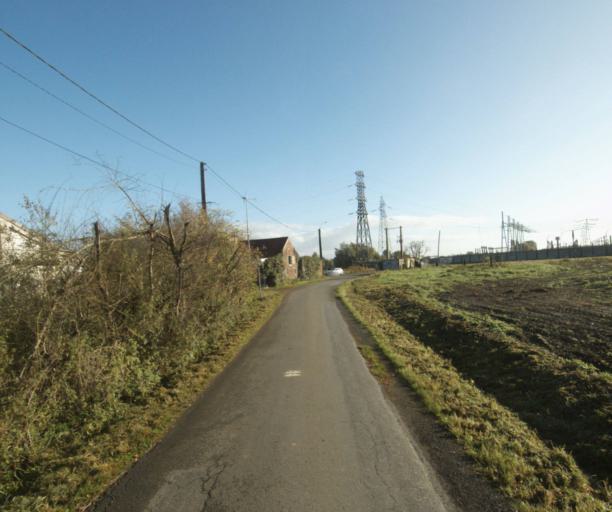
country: FR
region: Nord-Pas-de-Calais
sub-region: Departement du Nord
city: Wambrechies
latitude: 50.6763
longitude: 3.0350
